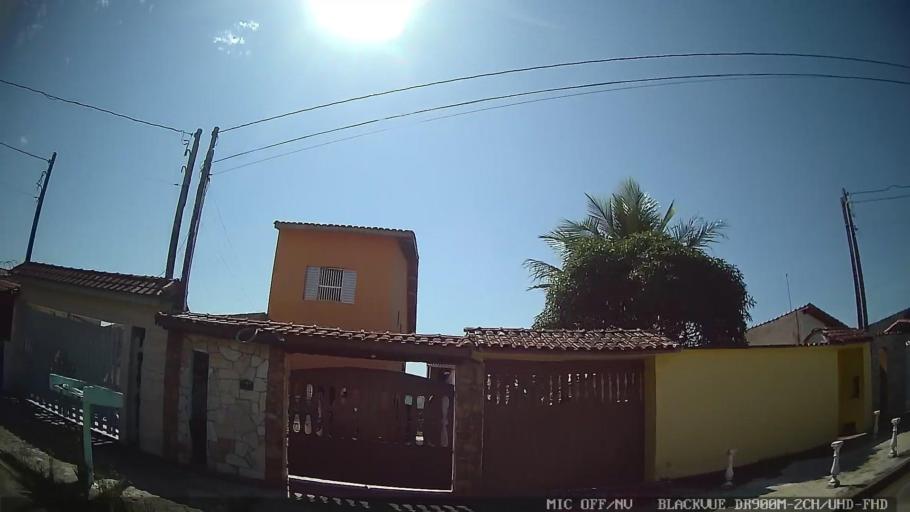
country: BR
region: Sao Paulo
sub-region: Itanhaem
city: Itanhaem
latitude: -24.2102
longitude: -46.8499
